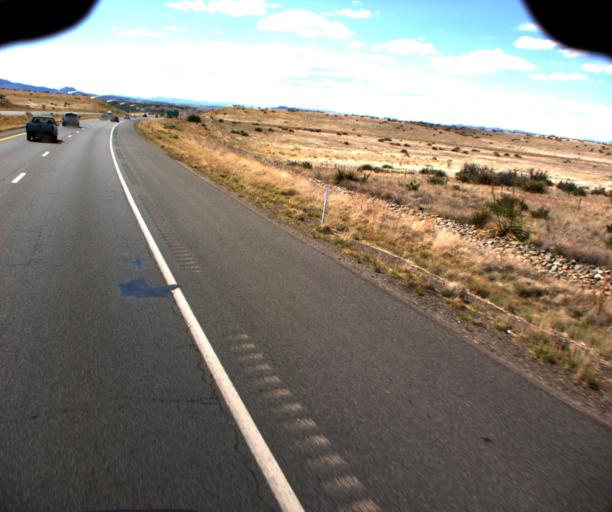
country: US
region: Arizona
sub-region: Yavapai County
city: Prescott Valley
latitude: 34.6316
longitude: -112.3876
